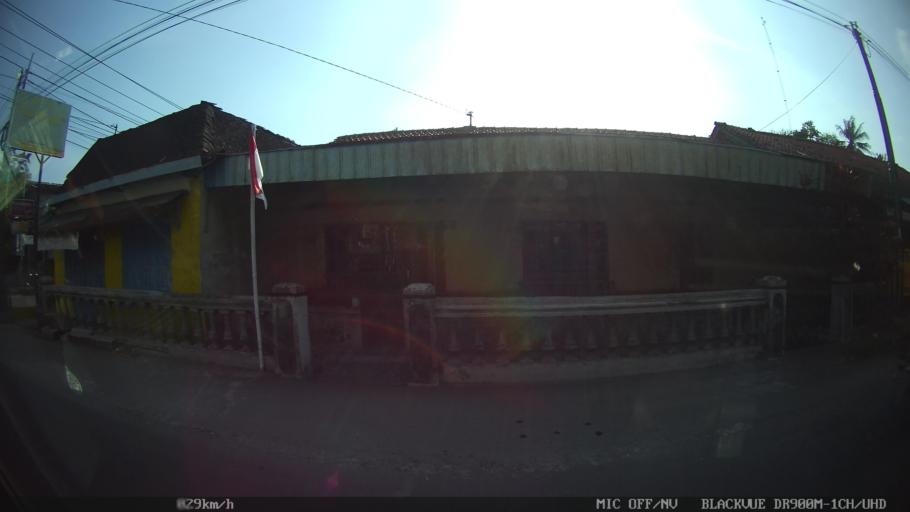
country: ID
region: Daerah Istimewa Yogyakarta
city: Pandak
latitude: -7.8973
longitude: 110.2982
